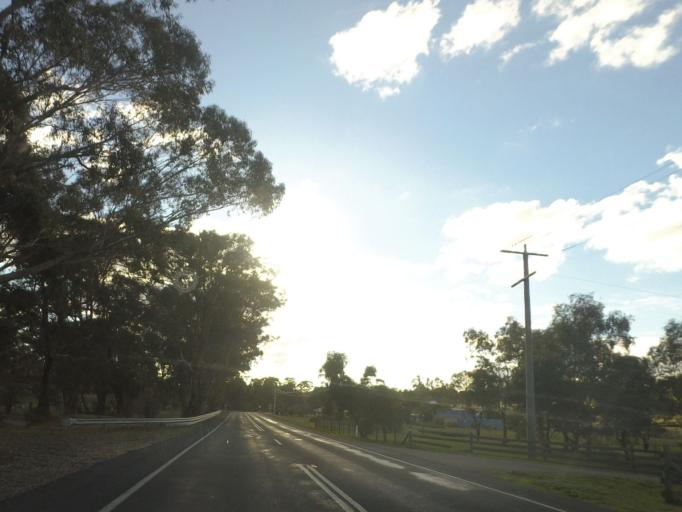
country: AU
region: Victoria
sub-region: Mount Alexander
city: Castlemaine
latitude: -37.0903
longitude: 144.2842
